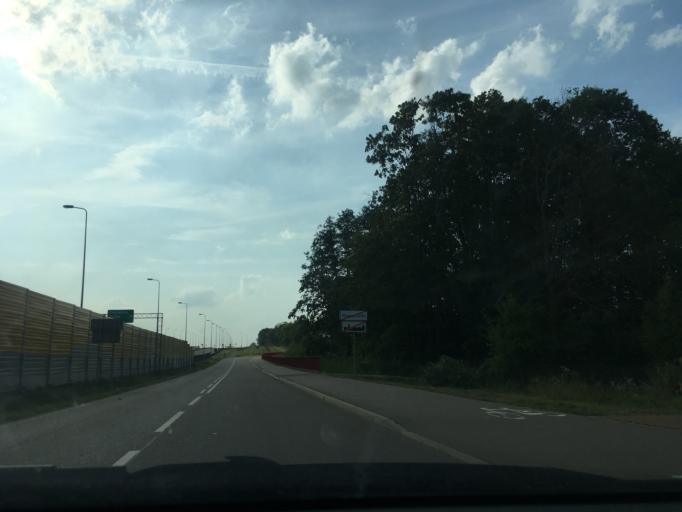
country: PL
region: Podlasie
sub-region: Powiat bialostocki
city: Choroszcz
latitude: 53.1580
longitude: 23.0064
